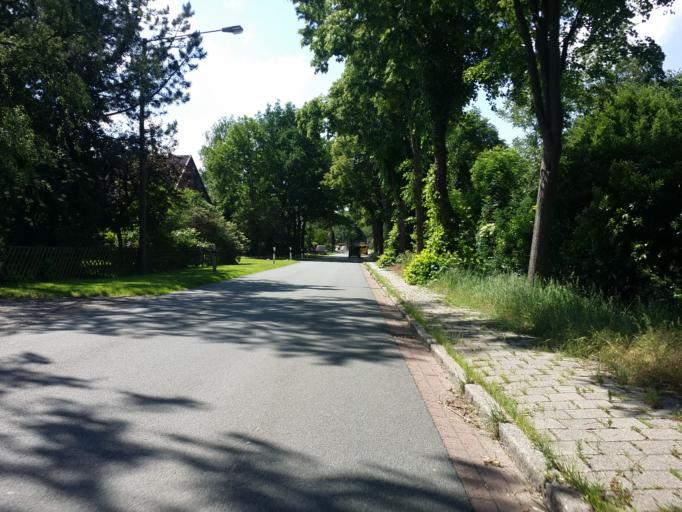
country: DE
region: Lower Saxony
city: Ritterhude
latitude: 53.1168
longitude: 8.6947
